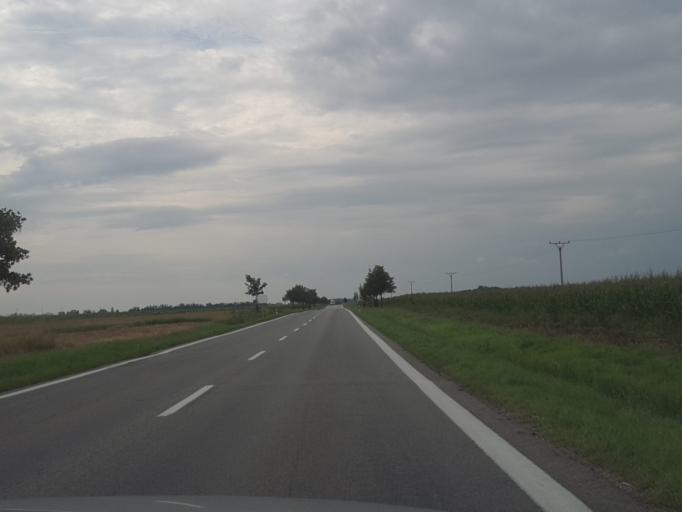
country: SK
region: Nitriansky
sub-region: Okres Nove Zamky
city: Nove Zamky
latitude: 48.0435
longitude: 18.1195
